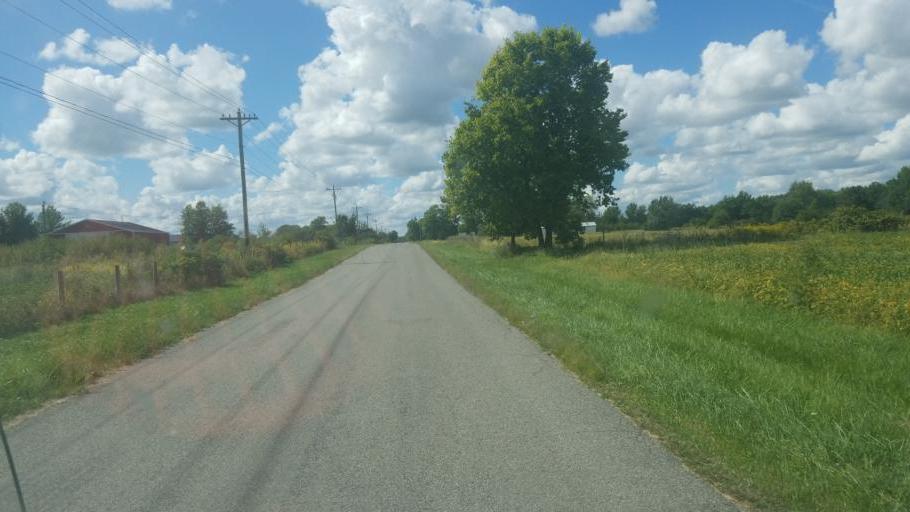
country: US
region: Ohio
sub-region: Champaign County
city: North Lewisburg
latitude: 40.3300
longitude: -83.4972
